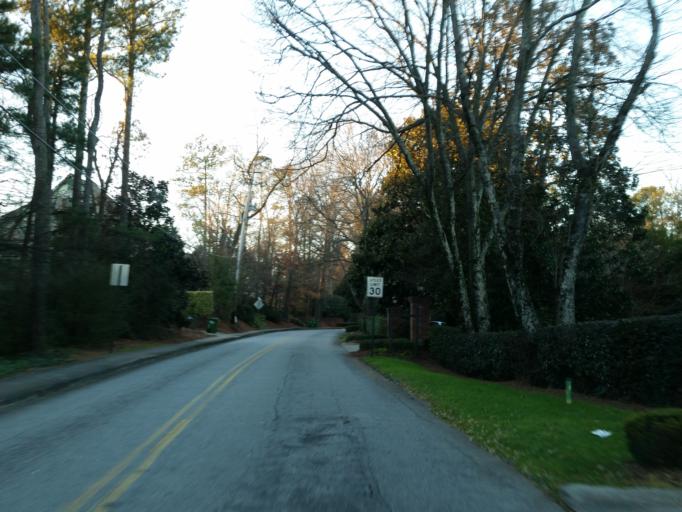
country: US
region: Georgia
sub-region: Cobb County
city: Vinings
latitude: 33.8143
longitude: -84.4271
